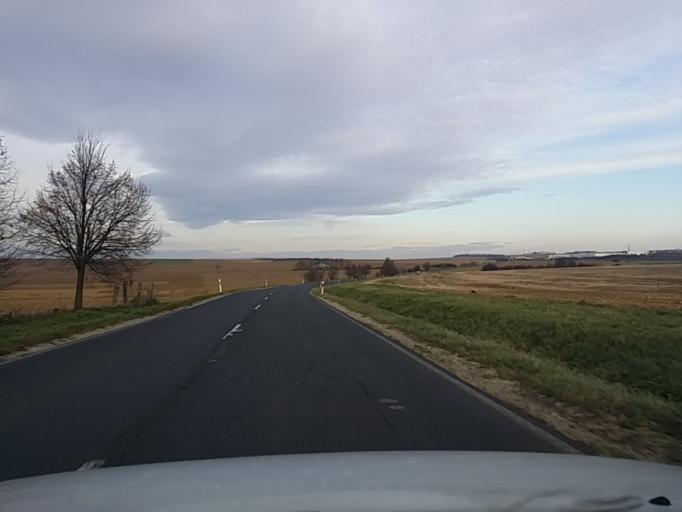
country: HU
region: Veszprem
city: Nemesvamos
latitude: 47.0527
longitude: 17.8429
